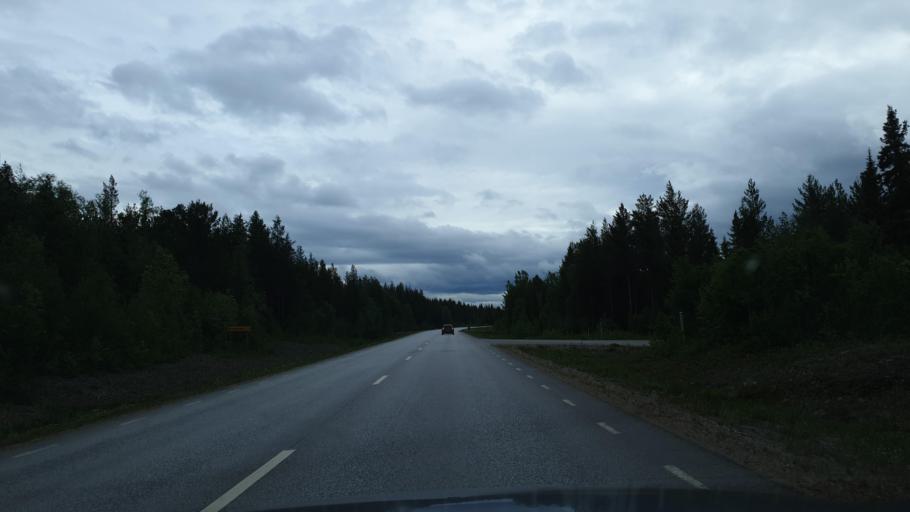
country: SE
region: Norrbotten
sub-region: Jokkmokks Kommun
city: Jokkmokk
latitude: 66.9808
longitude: 19.8354
